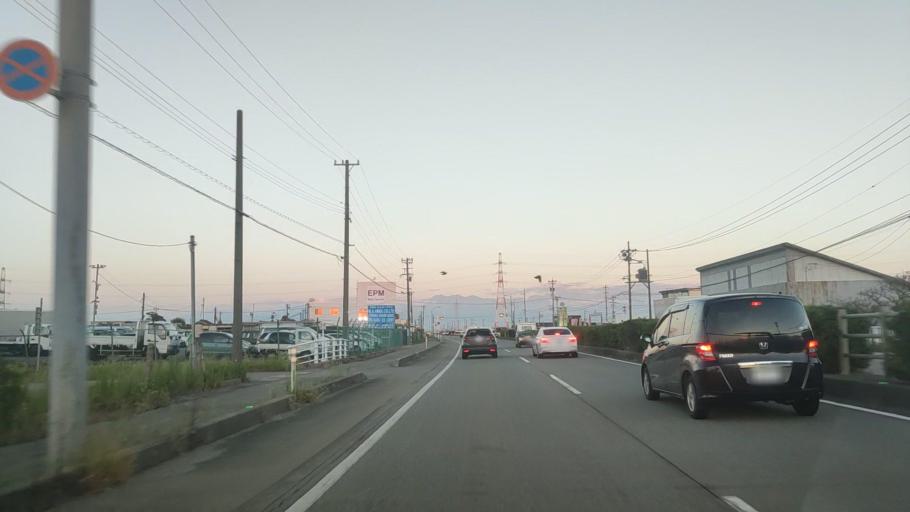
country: JP
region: Toyama
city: Kuragaki-kosugi
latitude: 36.7265
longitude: 137.1311
